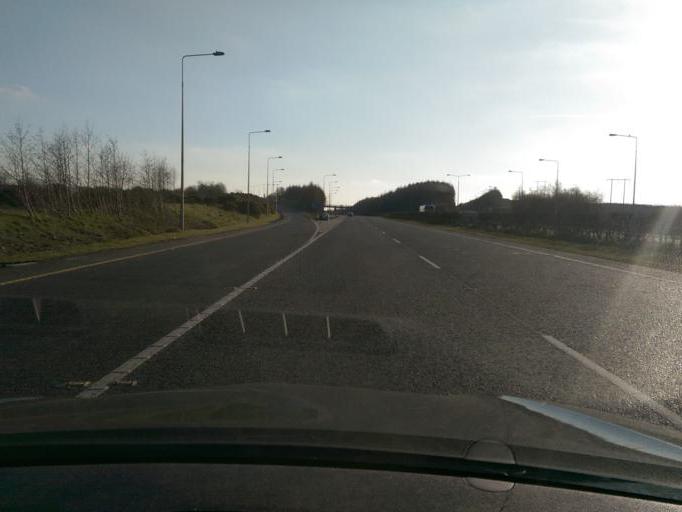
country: IE
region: Leinster
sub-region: Laois
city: Portlaoise
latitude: 53.0541
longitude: -7.2348
